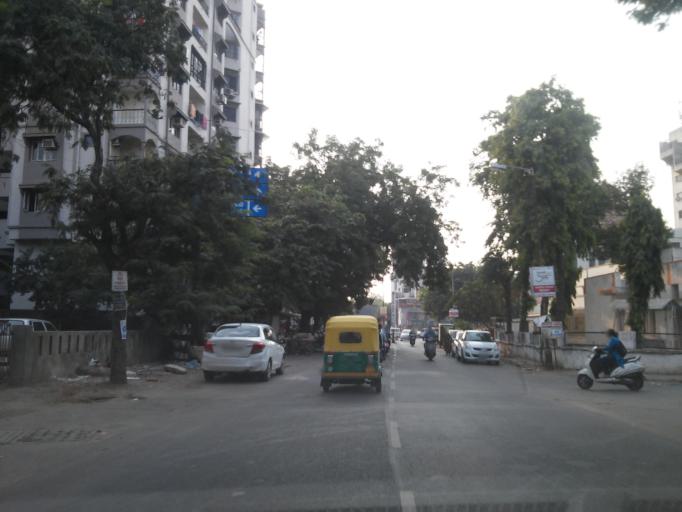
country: IN
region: Gujarat
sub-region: Ahmadabad
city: Ahmedabad
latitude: 23.0094
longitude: 72.5494
